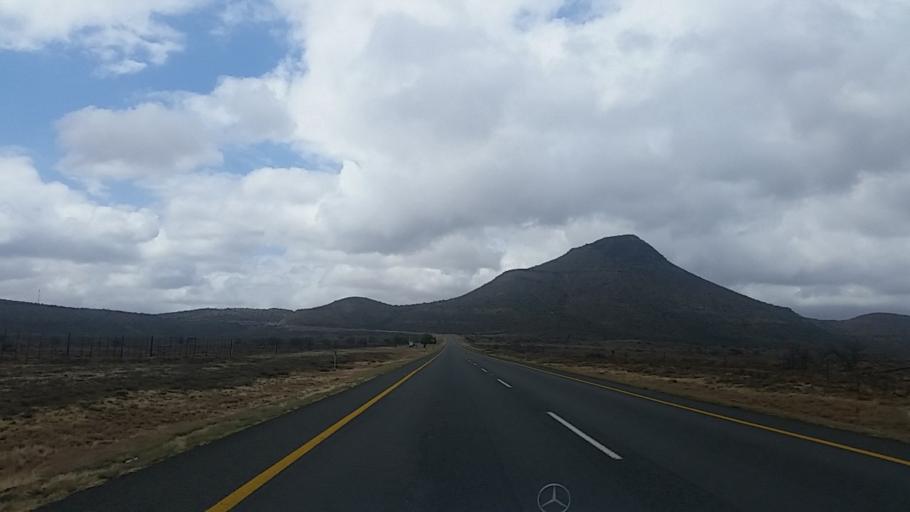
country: ZA
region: Eastern Cape
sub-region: Cacadu District Municipality
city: Graaff-Reinet
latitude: -32.1251
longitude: 24.5967
